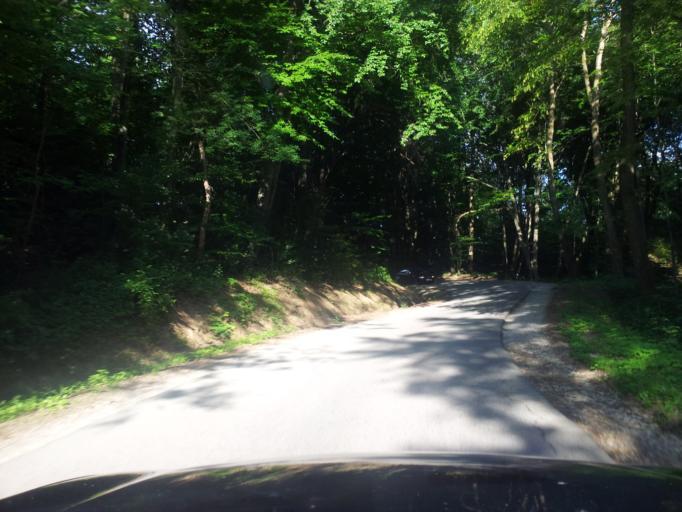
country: HR
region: Karlovacka
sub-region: Grad Karlovac
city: Karlovac
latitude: 45.4663
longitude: 15.4766
